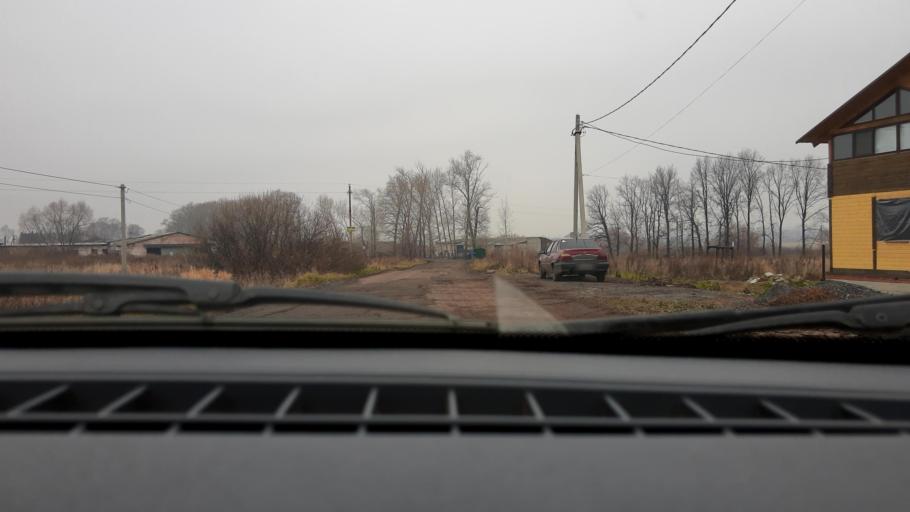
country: RU
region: Bashkortostan
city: Mikhaylovka
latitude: 54.8571
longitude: 55.8185
